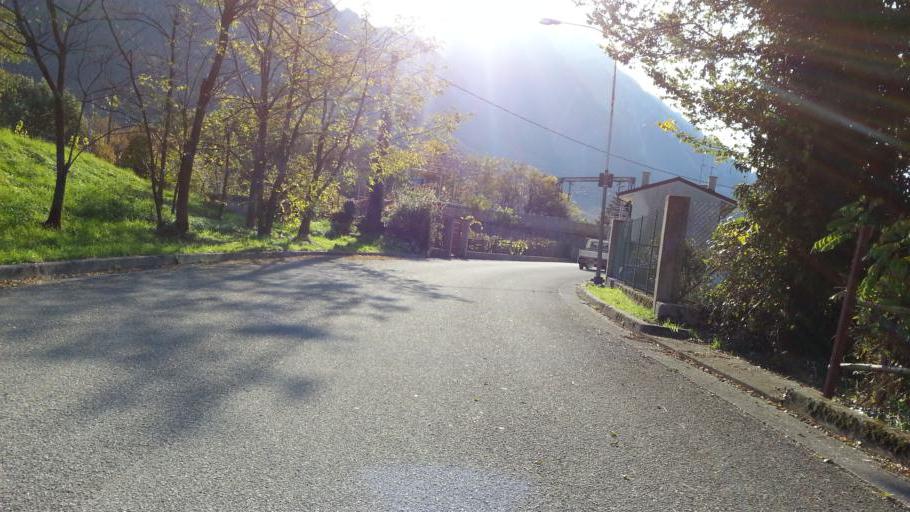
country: IT
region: Friuli Venezia Giulia
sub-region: Provincia di Udine
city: Venzone
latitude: 46.3336
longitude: 13.1355
